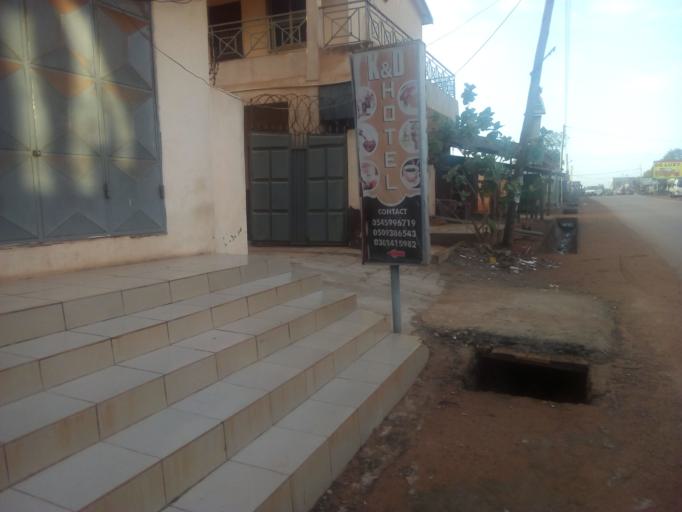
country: GH
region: Greater Accra
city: Dome
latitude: 5.6232
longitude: -0.2619
